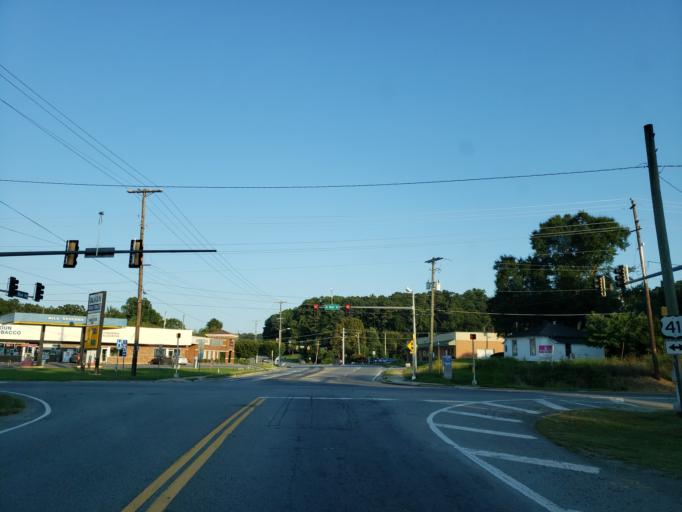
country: US
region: Georgia
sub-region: Gordon County
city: Calhoun
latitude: 34.5151
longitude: -84.9471
